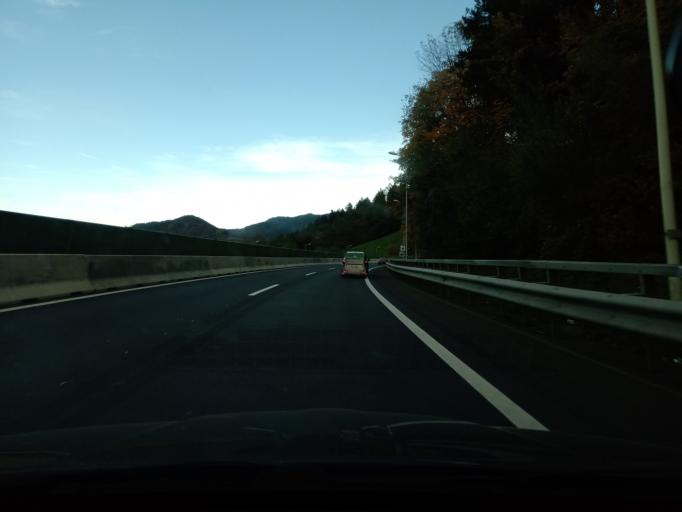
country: AT
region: Styria
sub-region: Politischer Bezirk Bruck-Muerzzuschlag
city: Bruck an der Mur
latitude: 47.4021
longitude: 15.2542
